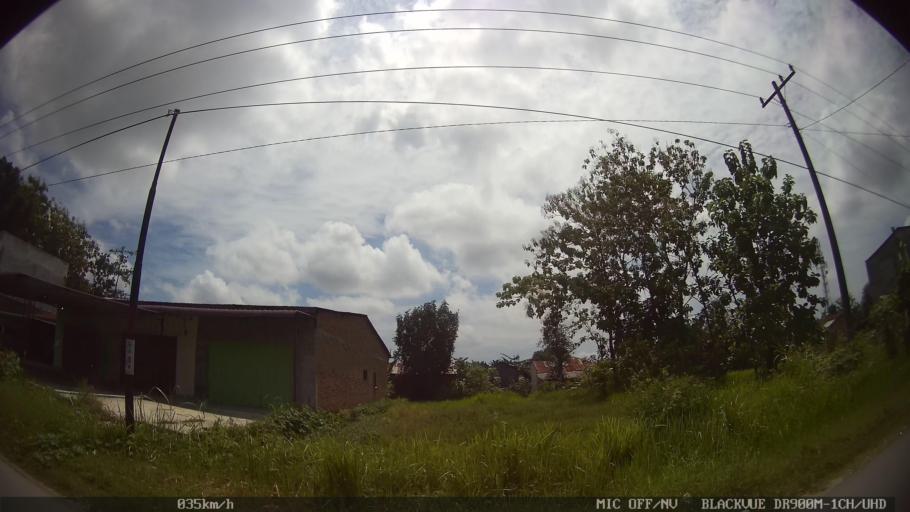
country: ID
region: North Sumatra
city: Percut
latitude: 3.6186
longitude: 98.7815
